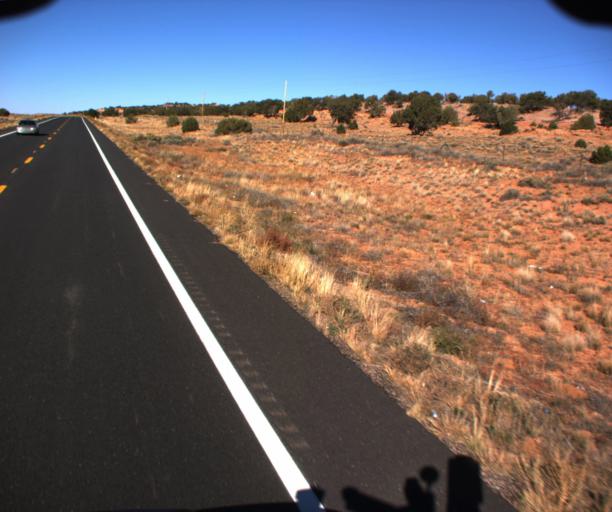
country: US
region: Arizona
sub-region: Coconino County
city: Kaibito
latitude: 36.5250
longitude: -110.7020
